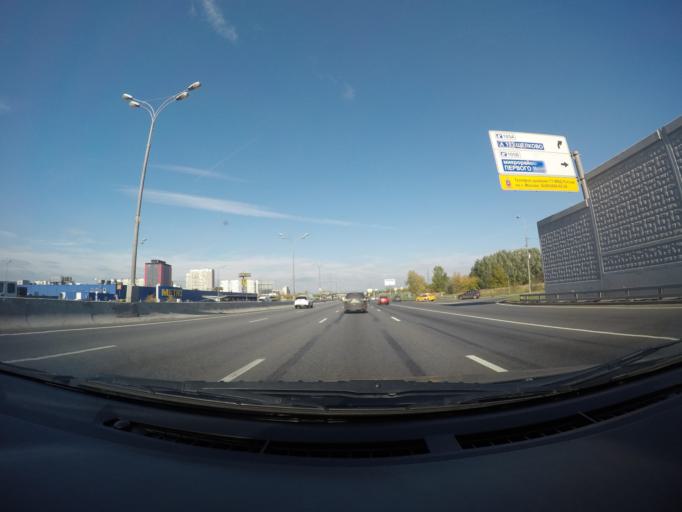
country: RU
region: Moscow
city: Vostochnyy
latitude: 55.8145
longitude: 37.8393
